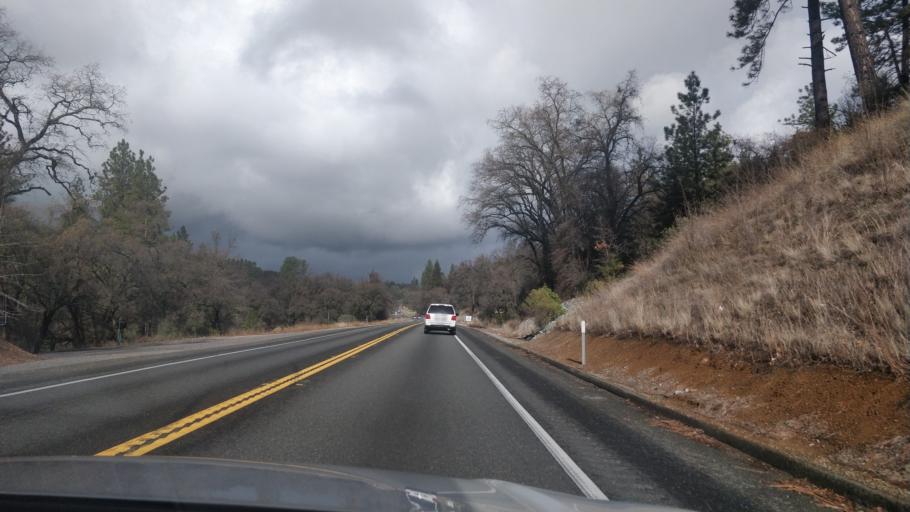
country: US
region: California
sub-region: Nevada County
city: Alta Sierra
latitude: 39.1188
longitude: -121.0798
